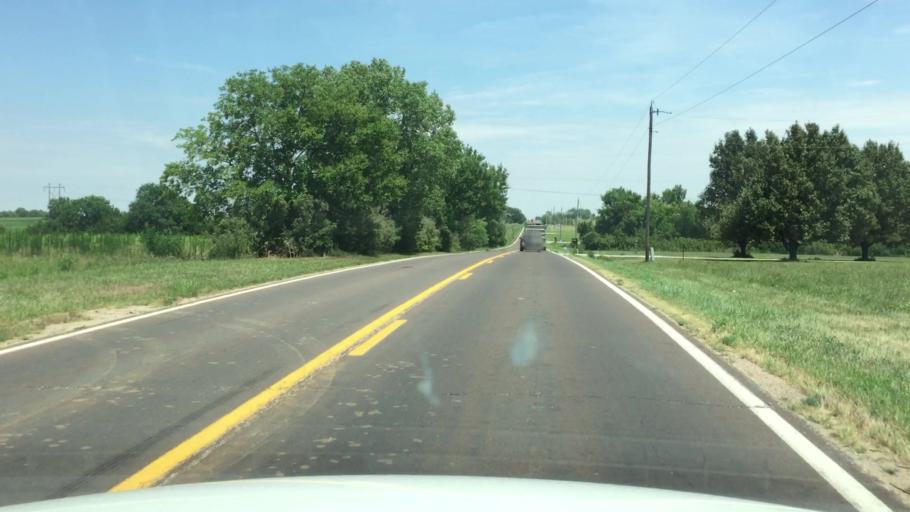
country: US
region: Kansas
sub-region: Shawnee County
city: Topeka
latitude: 38.9861
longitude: -95.6078
